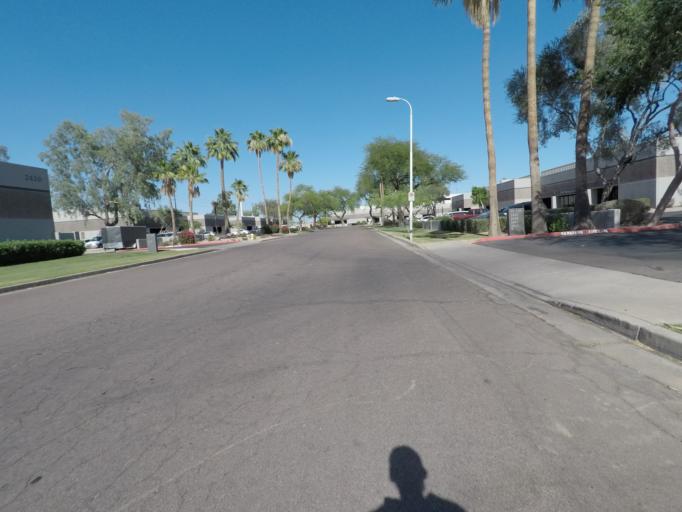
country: US
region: Arizona
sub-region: Maricopa County
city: Tempe Junction
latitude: 33.4159
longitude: -111.9760
